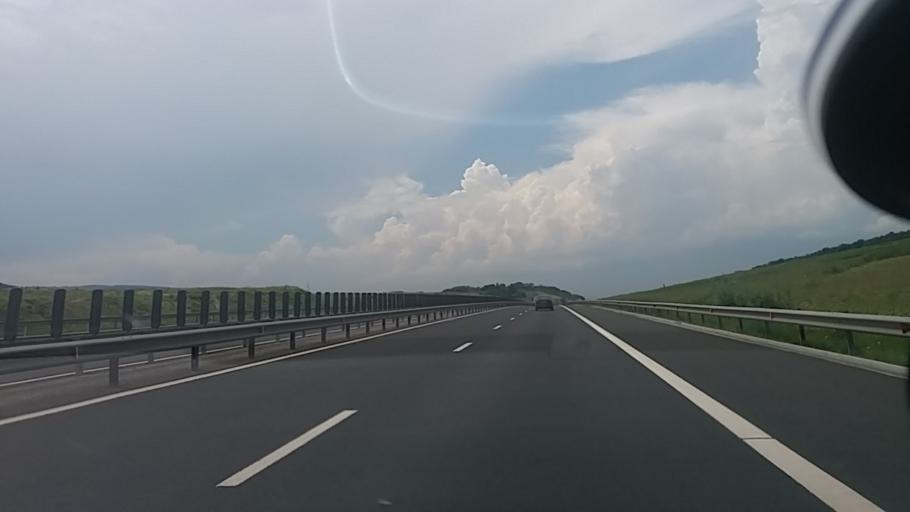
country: RO
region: Sibiu
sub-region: Oras Saliste
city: Saliste
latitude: 45.8145
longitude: 23.8869
